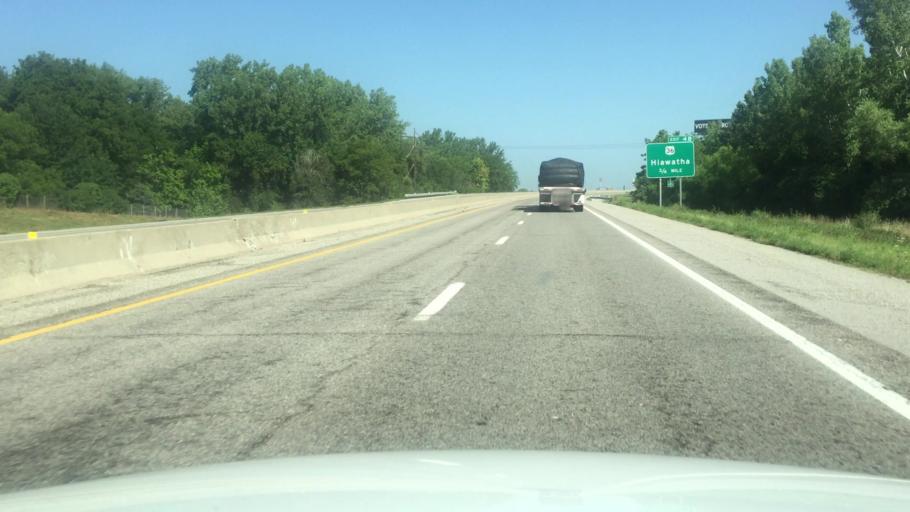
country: US
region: Kansas
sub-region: Doniphan County
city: Elwood
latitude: 39.7341
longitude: -94.8490
